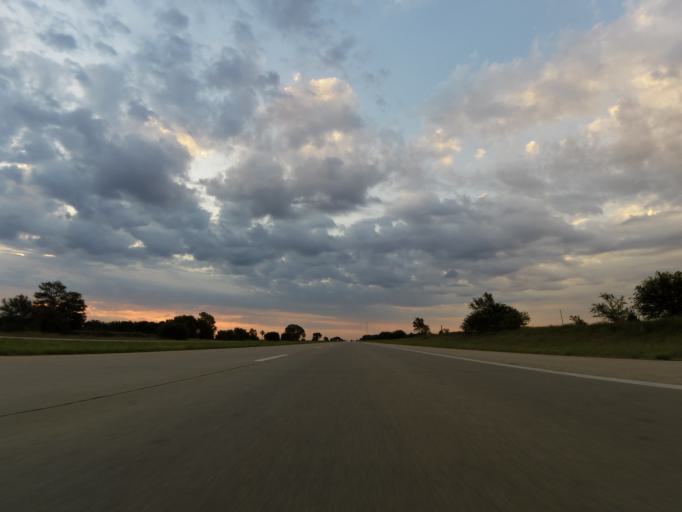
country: US
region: Kansas
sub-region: Reno County
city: Haven
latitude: 37.9194
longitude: -97.8285
